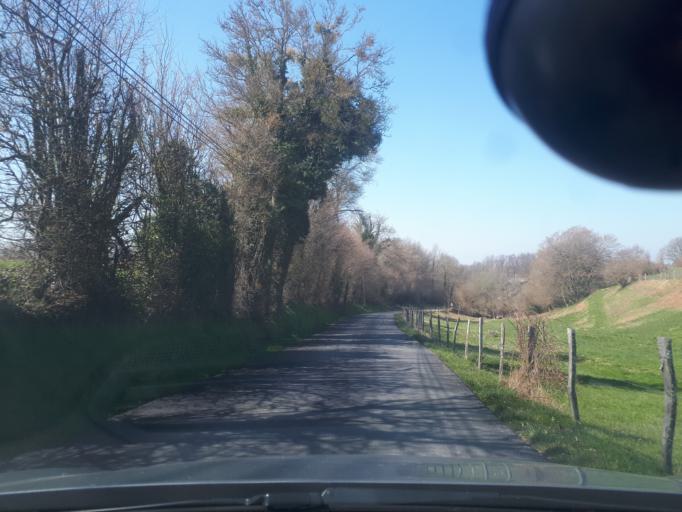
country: FR
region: Rhone-Alpes
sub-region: Departement de l'Isere
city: Cessieu
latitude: 45.5225
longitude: 5.3485
